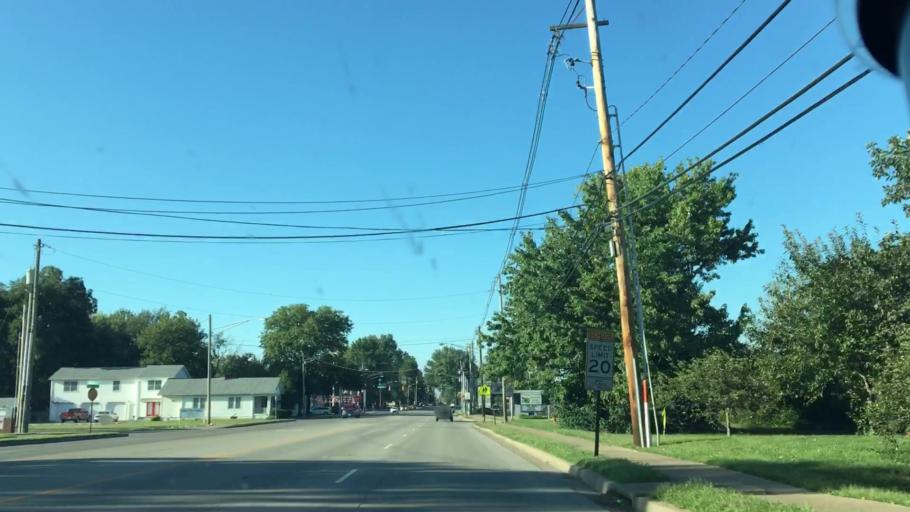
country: US
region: Indiana
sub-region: Vanderburgh County
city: Evansville
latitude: 37.9455
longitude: -87.4929
